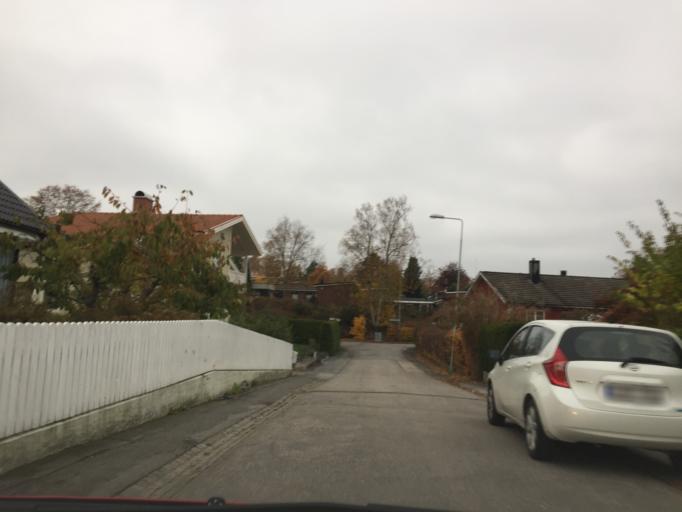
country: SE
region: Vaestra Goetaland
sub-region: Trollhattan
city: Trollhattan
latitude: 58.2663
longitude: 12.2790
